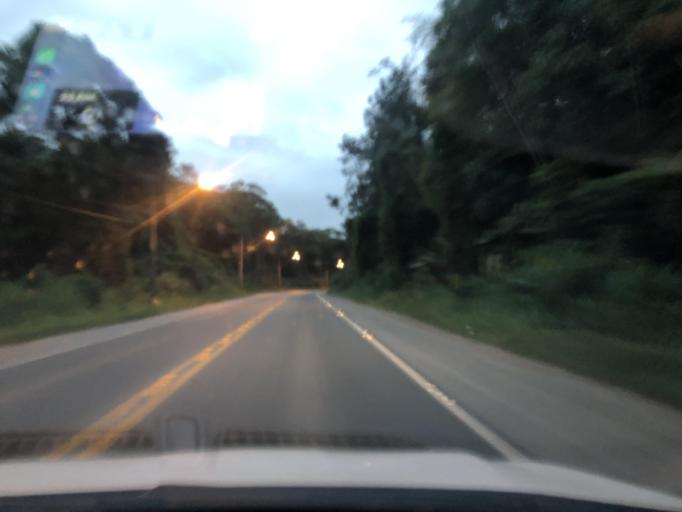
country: BR
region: Santa Catarina
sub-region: Pomerode
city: Pomerode
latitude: -26.7290
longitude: -49.0645
